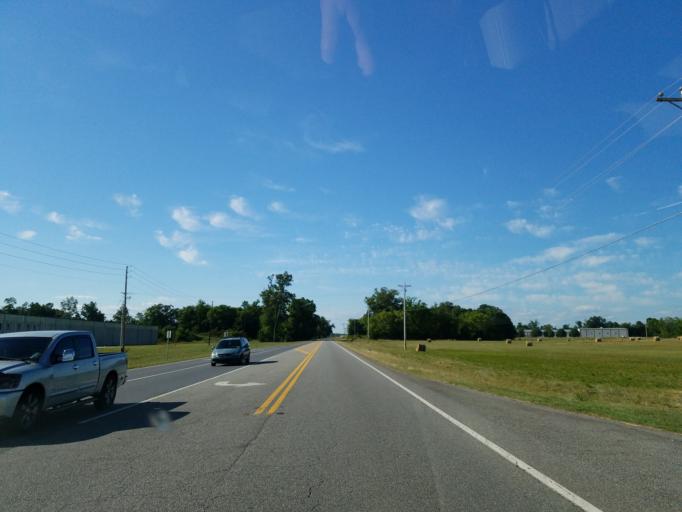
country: US
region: Georgia
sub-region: Gordon County
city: Calhoun
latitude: 34.4374
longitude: -84.9353
